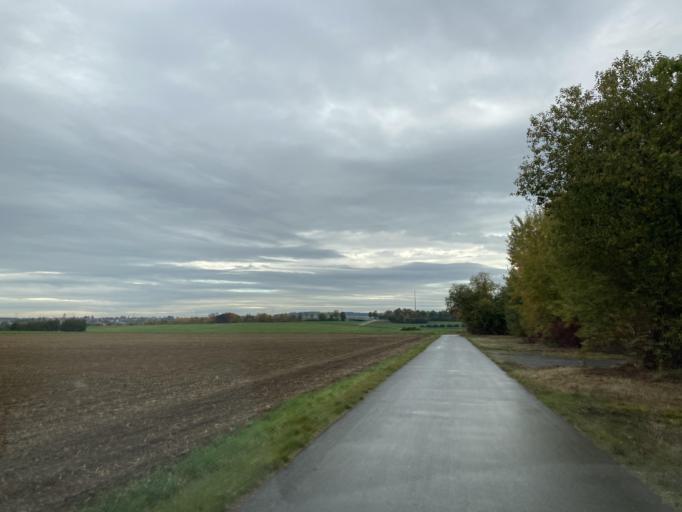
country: DE
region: Baden-Wuerttemberg
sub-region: Regierungsbezirk Stuttgart
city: Bondorf
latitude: 48.5371
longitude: 8.8535
